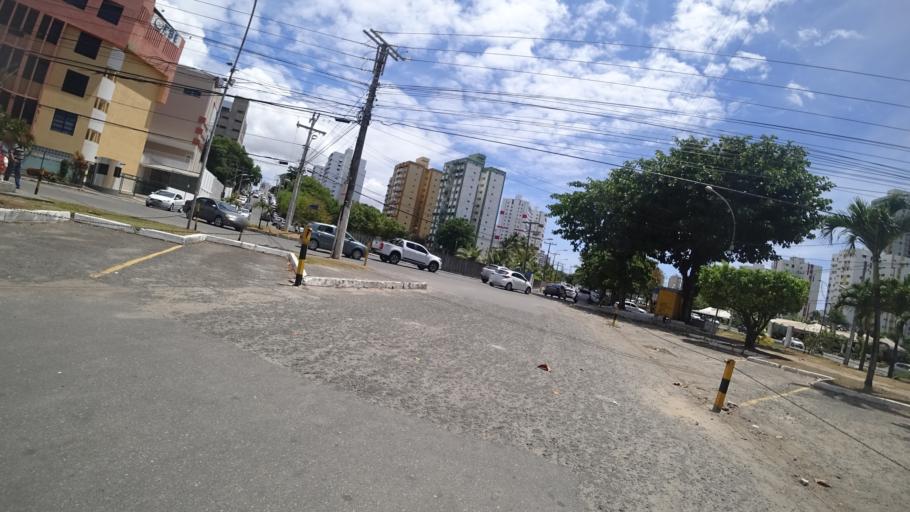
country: BR
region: Bahia
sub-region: Salvador
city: Salvador
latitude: -12.9688
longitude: -38.4379
